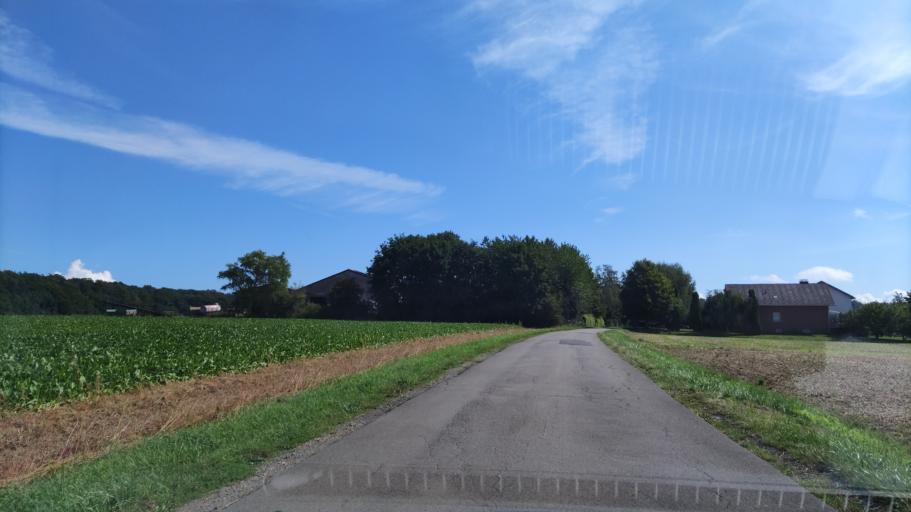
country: DE
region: Lower Saxony
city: Bad Karlshafen
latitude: 51.6591
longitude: 9.4278
